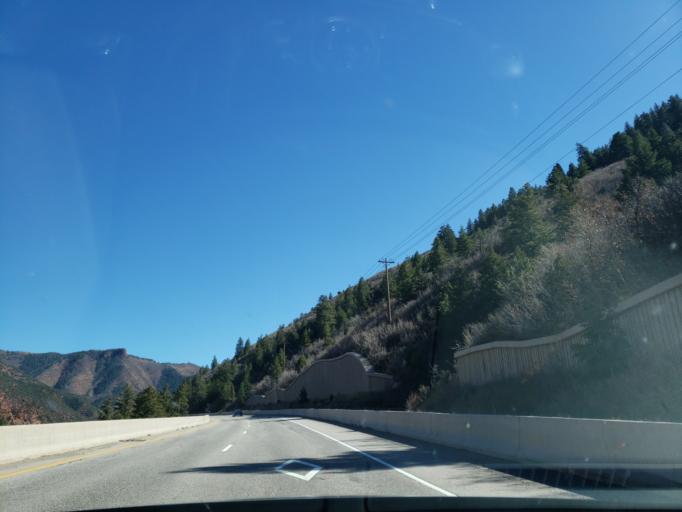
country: US
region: Colorado
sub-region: Eagle County
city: Basalt
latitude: 39.3291
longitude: -106.9719
